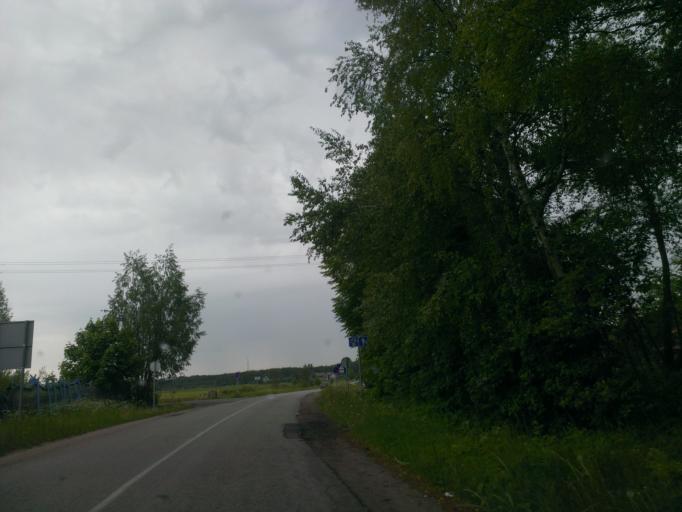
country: LT
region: Klaipedos apskritis
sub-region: Klaipeda
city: Klaipeda
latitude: 55.8061
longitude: 21.0753
